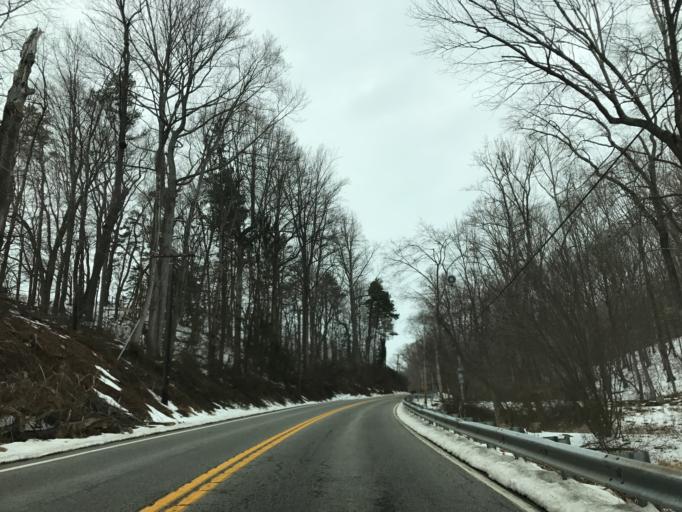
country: US
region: Maryland
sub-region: Harford County
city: Jarrettsville
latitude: 39.6521
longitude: -76.4101
